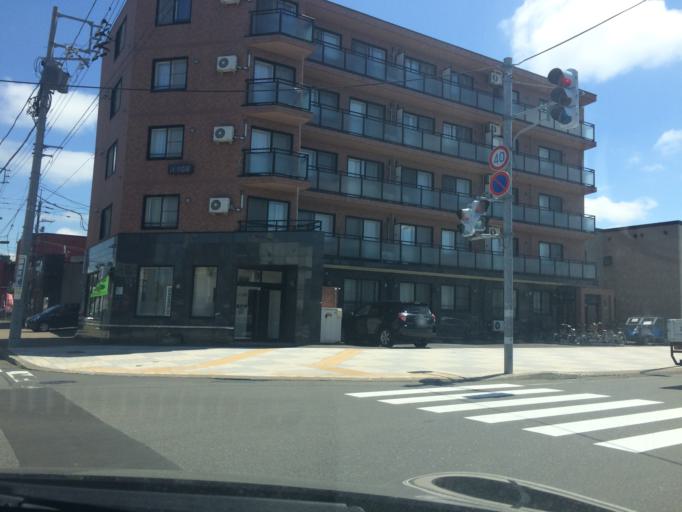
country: JP
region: Hokkaido
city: Tobetsu
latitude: 43.2198
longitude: 141.5152
